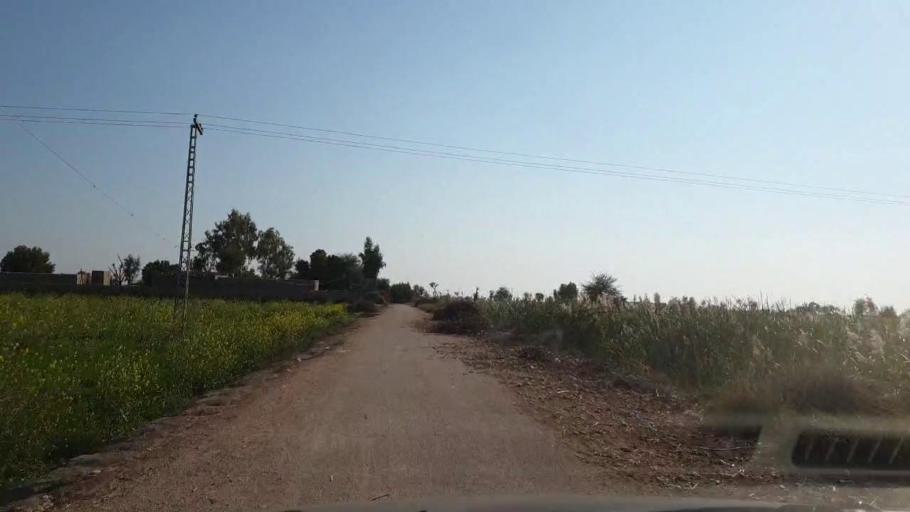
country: PK
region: Sindh
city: Khadro
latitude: 26.1530
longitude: 68.7690
